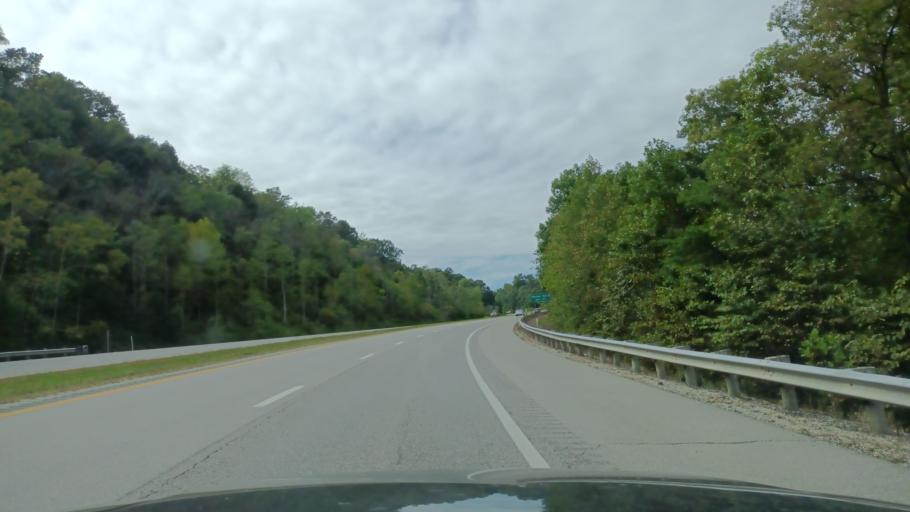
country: US
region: Ohio
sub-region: Washington County
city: Reno
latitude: 39.2410
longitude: -81.4056
